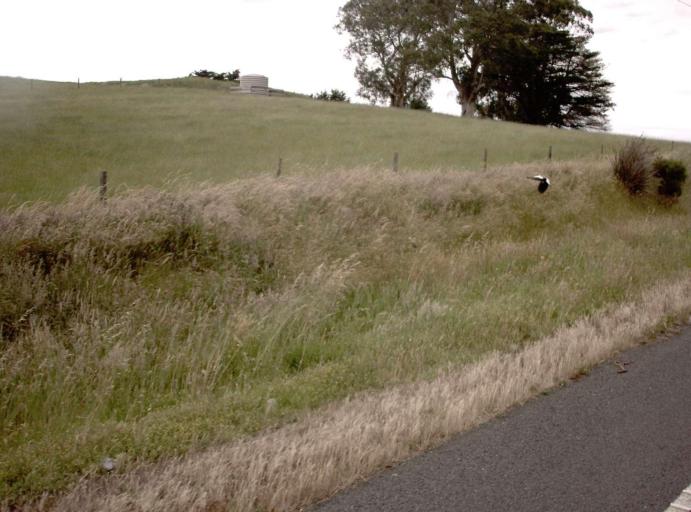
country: AU
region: Victoria
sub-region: Baw Baw
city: Warragul
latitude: -38.4490
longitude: 145.8857
